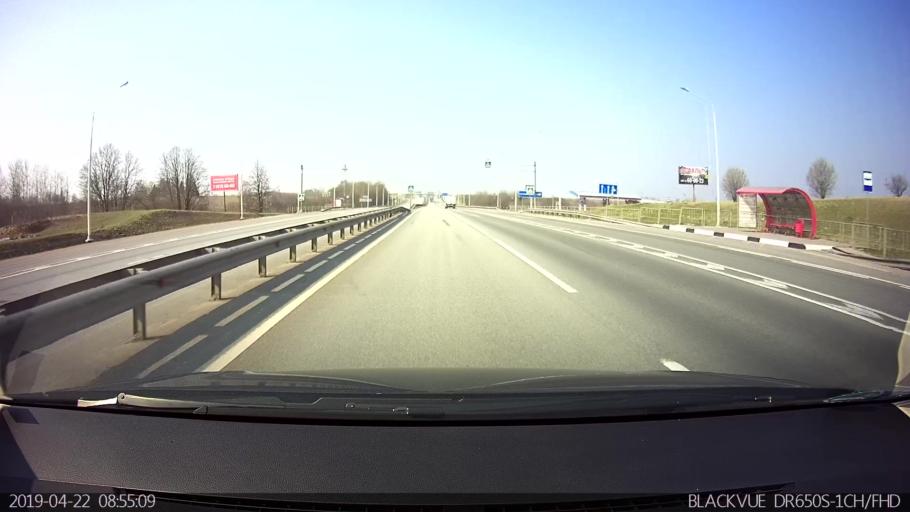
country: RU
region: Smolensk
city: Pechersk
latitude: 54.8841
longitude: 32.0745
